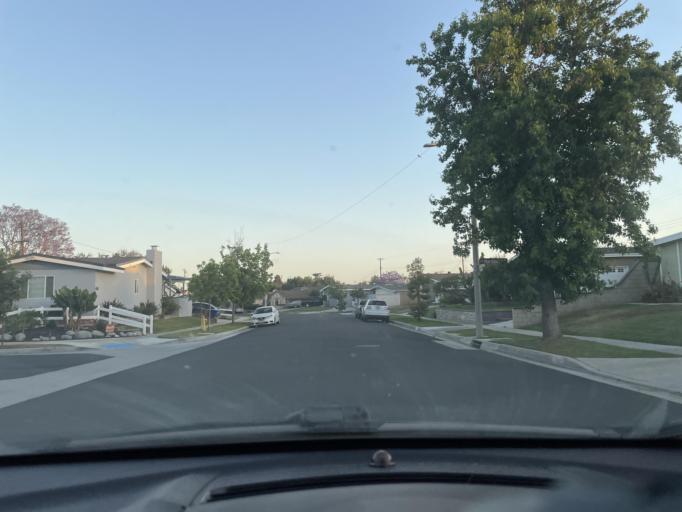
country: US
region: California
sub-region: Los Angeles County
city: La Mirada
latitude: 33.9080
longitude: -118.0246
